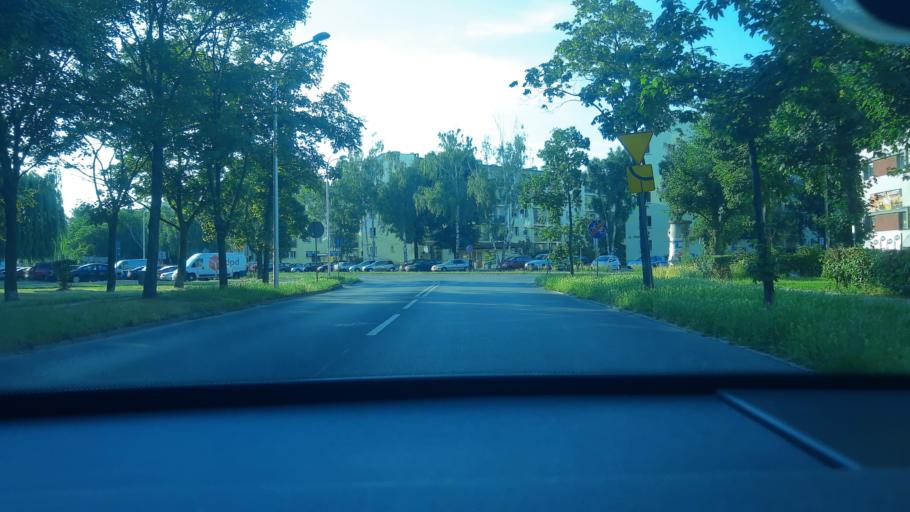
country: PL
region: Lodz Voivodeship
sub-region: Powiat sieradzki
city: Sieradz
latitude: 51.5891
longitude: 18.7313
